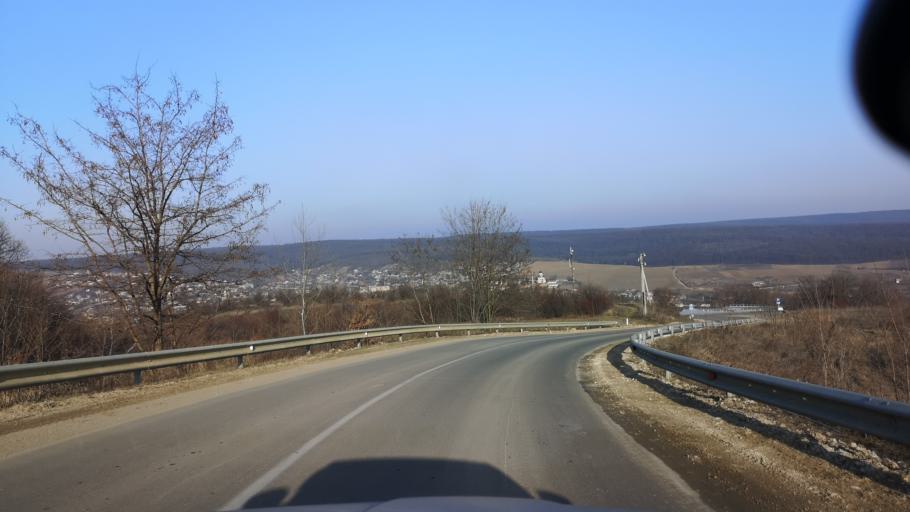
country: MD
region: Stinga Nistrului
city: Bucovat
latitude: 47.1051
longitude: 28.4962
